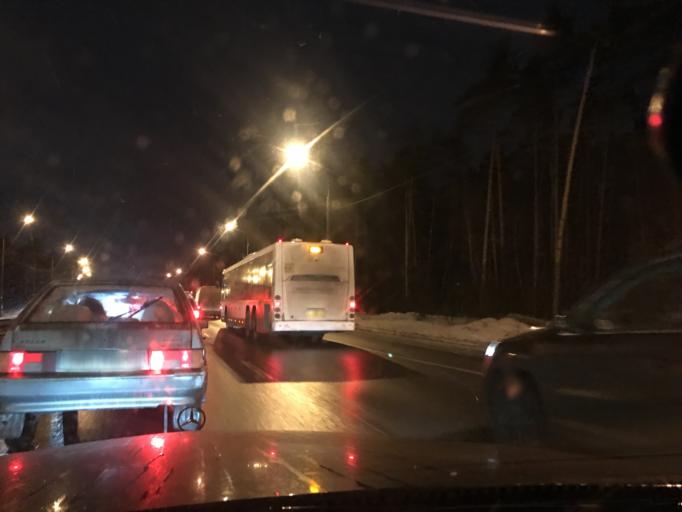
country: RU
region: Moskovskaya
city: Monino
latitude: 55.8254
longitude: 38.2175
